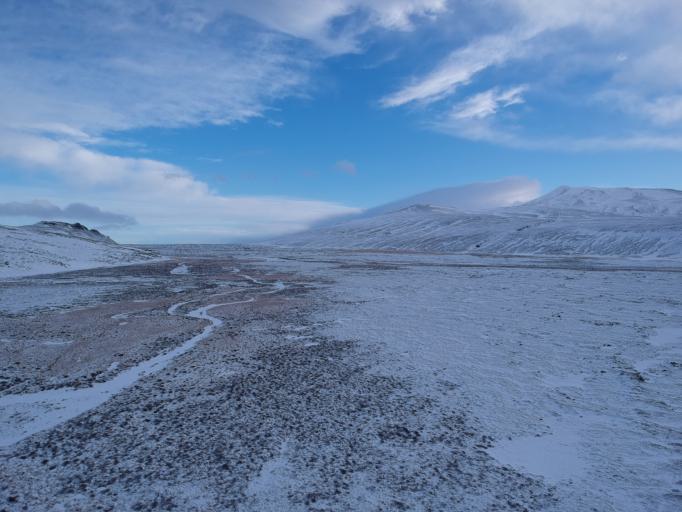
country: IS
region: South
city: Selfoss
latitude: 64.7531
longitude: -20.8014
